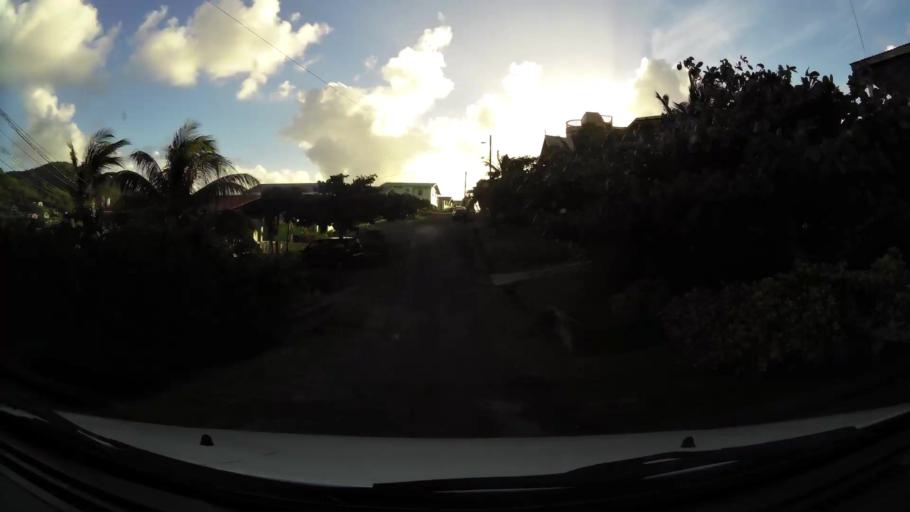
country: LC
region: Gros-Islet
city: Gros Islet
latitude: 14.0758
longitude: -60.9278
